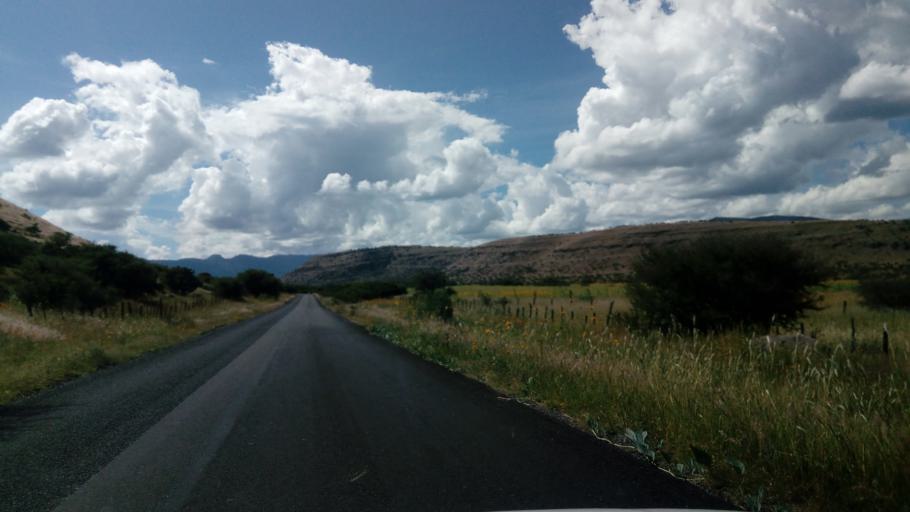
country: MX
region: Durango
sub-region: Durango
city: Jose Refugio Salcido
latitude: 23.8318
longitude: -104.4814
